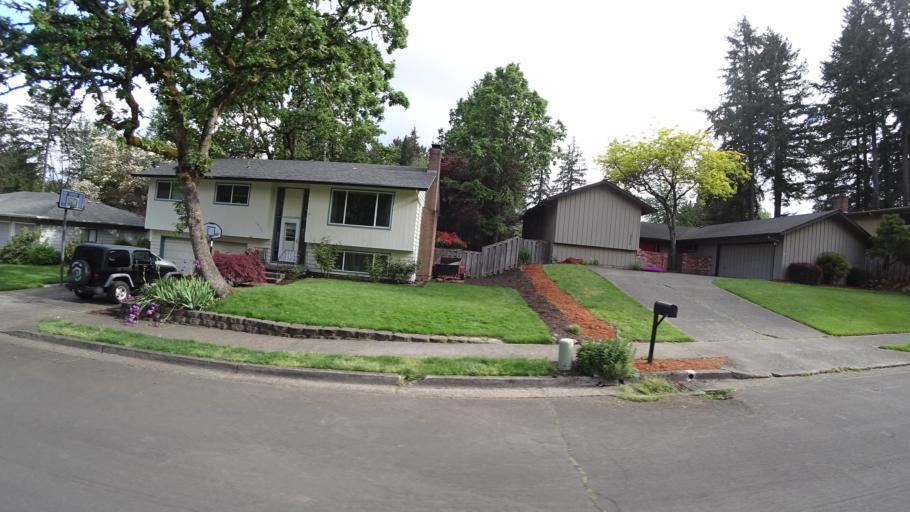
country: US
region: Oregon
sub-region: Washington County
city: Beaverton
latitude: 45.4677
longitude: -122.8222
